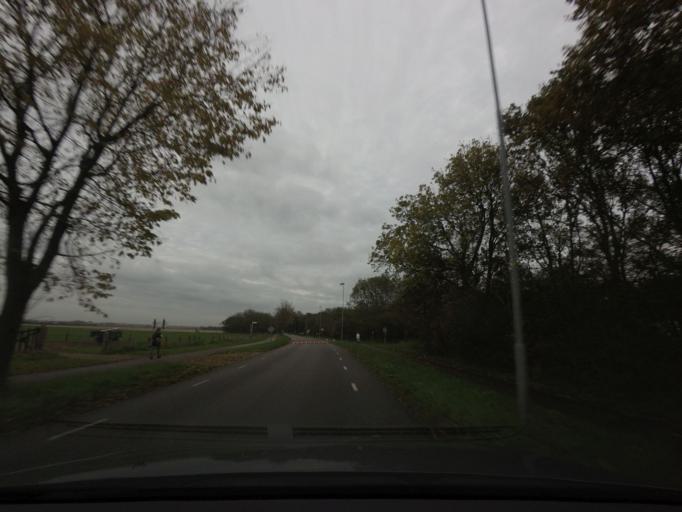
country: NL
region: North Holland
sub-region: Gemeente Heiloo
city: Heiloo
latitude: 52.6127
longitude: 4.6588
